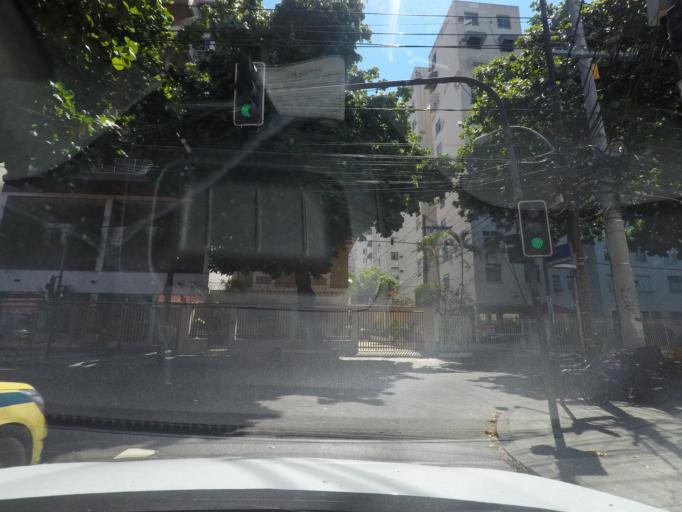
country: BR
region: Rio de Janeiro
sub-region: Rio De Janeiro
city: Rio de Janeiro
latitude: -22.9202
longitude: -43.2398
